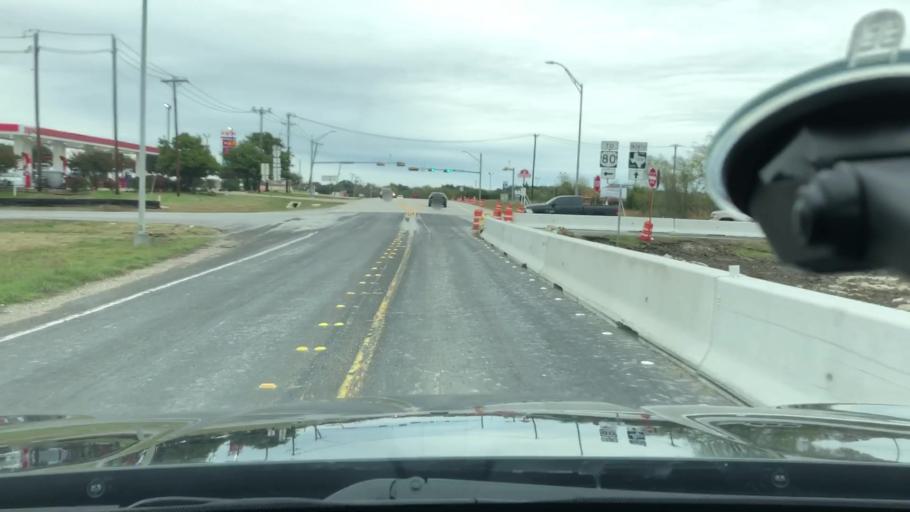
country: US
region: Texas
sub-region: Kaufman County
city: Terrell
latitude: 32.7221
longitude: -96.3182
